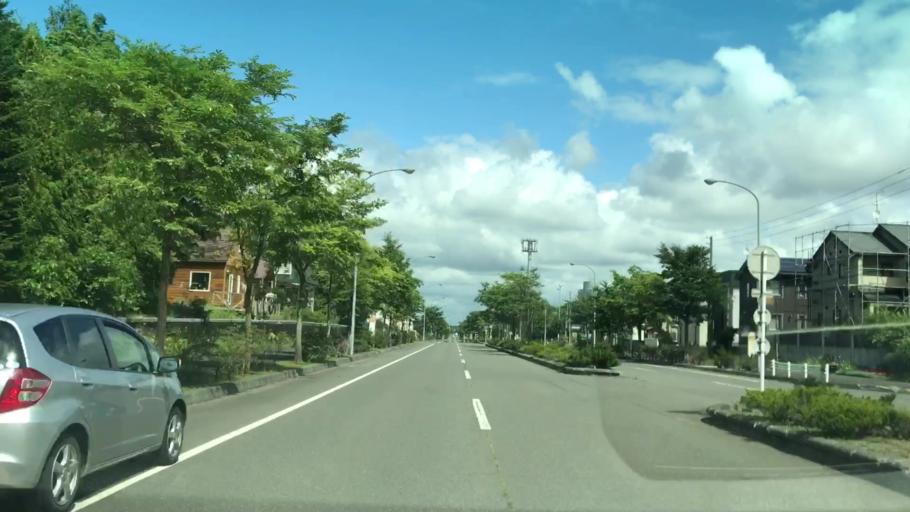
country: JP
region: Hokkaido
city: Chitose
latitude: 42.7757
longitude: 141.5995
